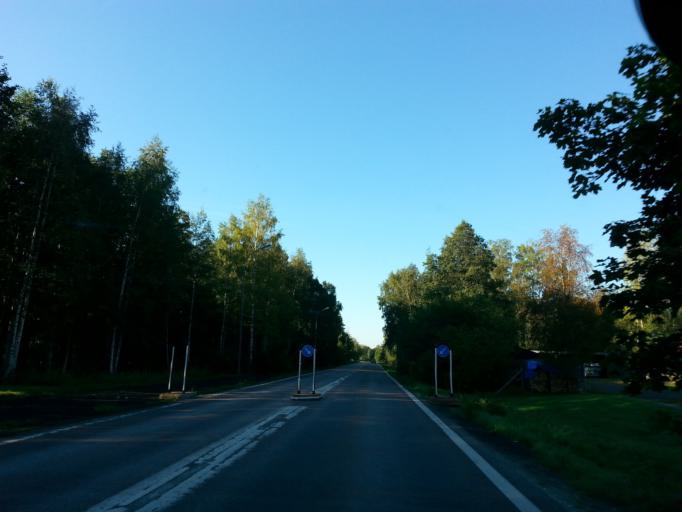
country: SE
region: Uppsala
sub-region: Osthammars Kommun
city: Oregrund
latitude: 60.3336
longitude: 18.4315
